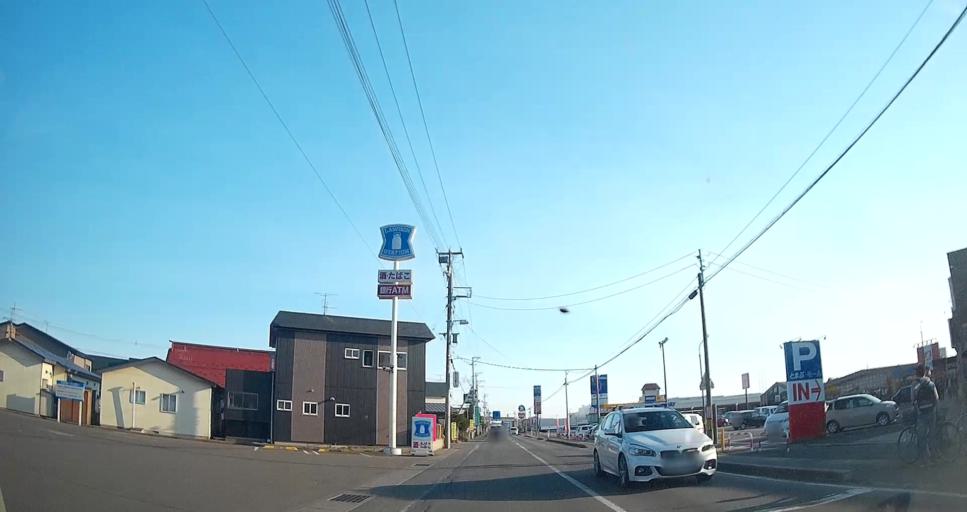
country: JP
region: Aomori
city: Mutsu
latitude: 41.2861
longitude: 141.2115
